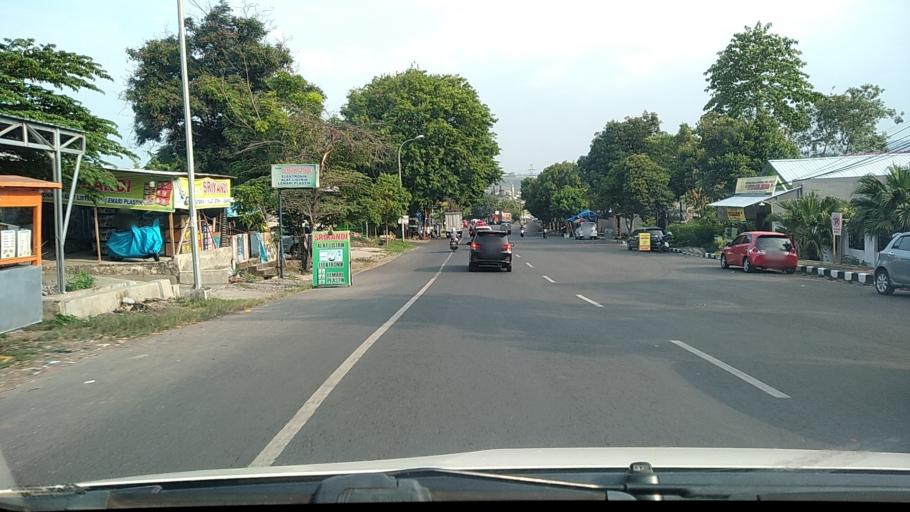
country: ID
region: Central Java
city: Semarang
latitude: -7.0006
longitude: 110.3908
